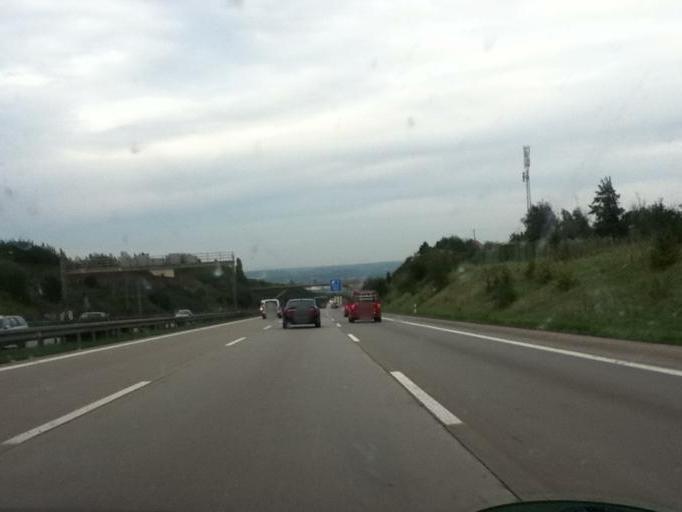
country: DE
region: Saxony
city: Radebeul
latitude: 51.0690
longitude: 13.6325
